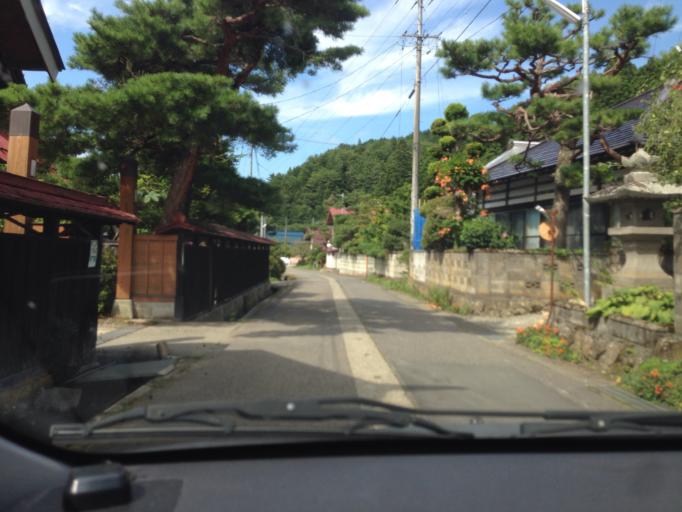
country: JP
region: Fukushima
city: Inawashiro
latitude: 37.3648
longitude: 140.0829
